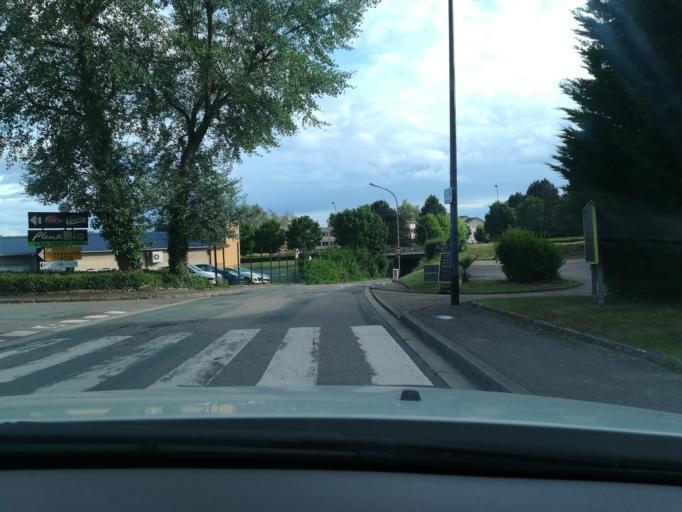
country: FR
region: Haute-Normandie
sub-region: Departement de la Seine-Maritime
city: Mont-Saint-Aignan
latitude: 49.4755
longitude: 1.1089
